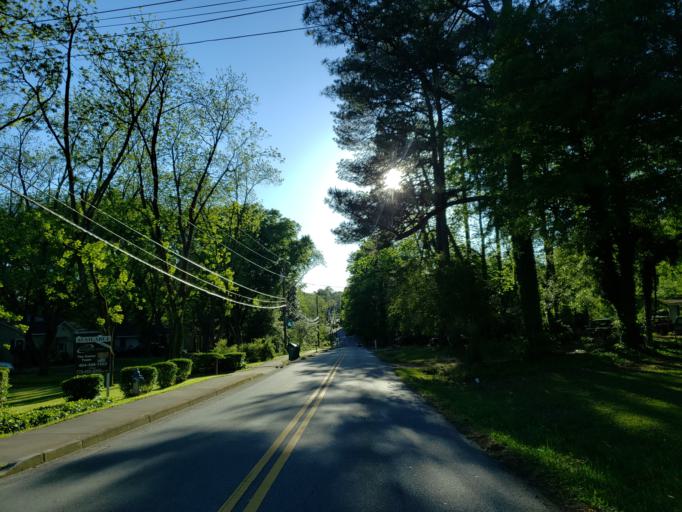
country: US
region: Georgia
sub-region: Cobb County
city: Smyrna
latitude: 33.9019
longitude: -84.5270
